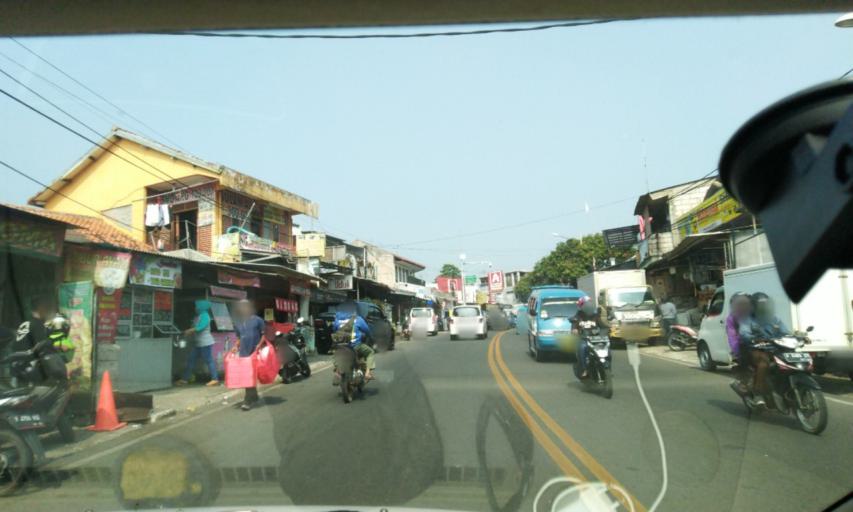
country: ID
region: West Java
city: Caringin
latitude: -6.6627
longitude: 106.8566
